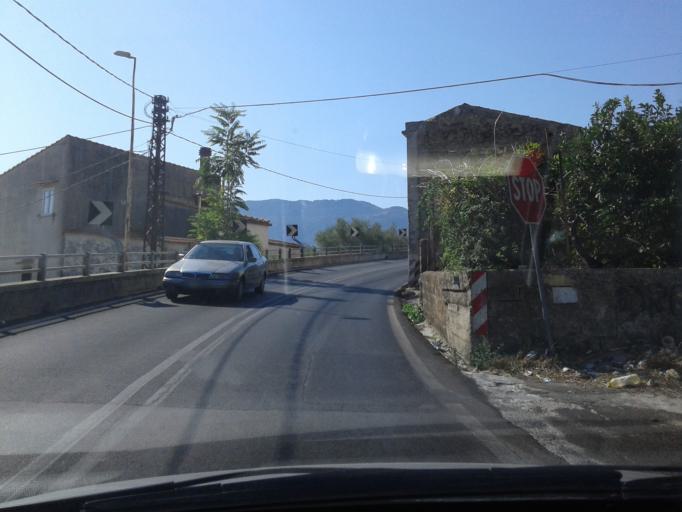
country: IT
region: Sicily
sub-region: Palermo
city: Cannizzaro-Favara
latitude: 38.0685
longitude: 13.2693
